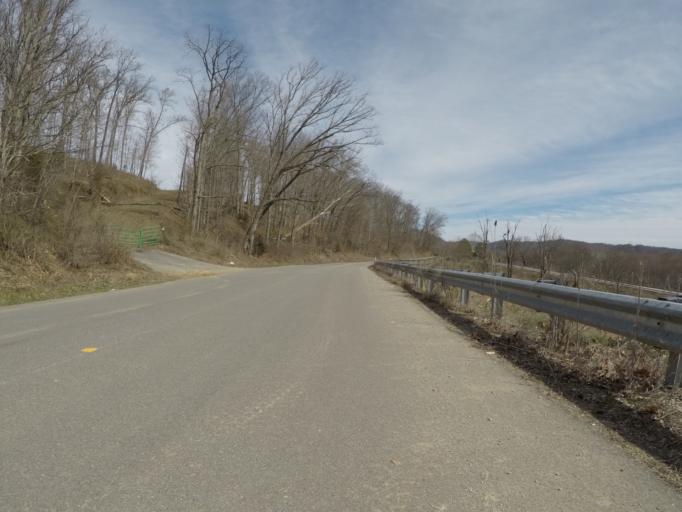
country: US
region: West Virginia
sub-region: Wayne County
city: Ceredo
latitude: 38.3734
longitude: -82.5409
